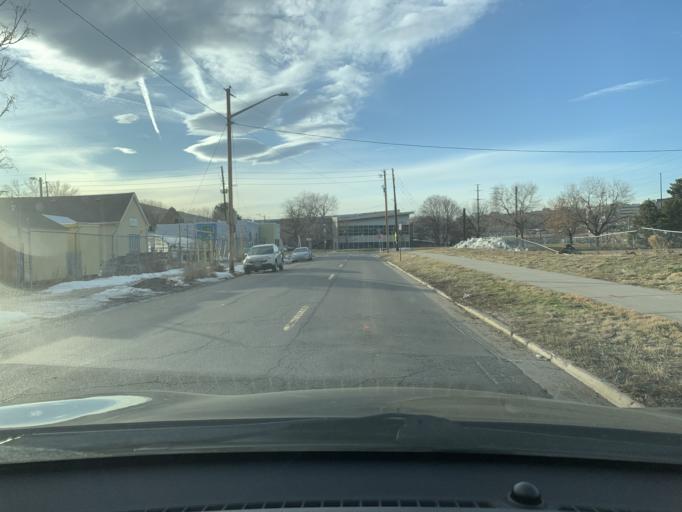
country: US
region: Colorado
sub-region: Denver County
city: Denver
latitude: 39.7365
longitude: -105.0207
